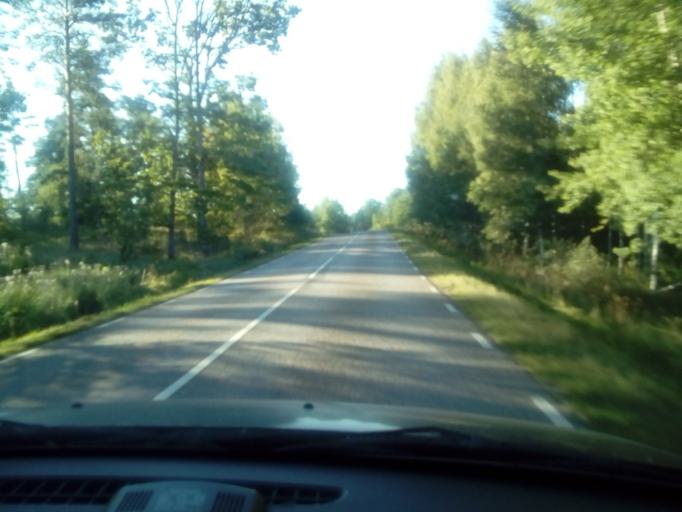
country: SE
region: Kalmar
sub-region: Vasterviks Kommun
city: Gamleby
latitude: 57.7918
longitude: 16.3797
